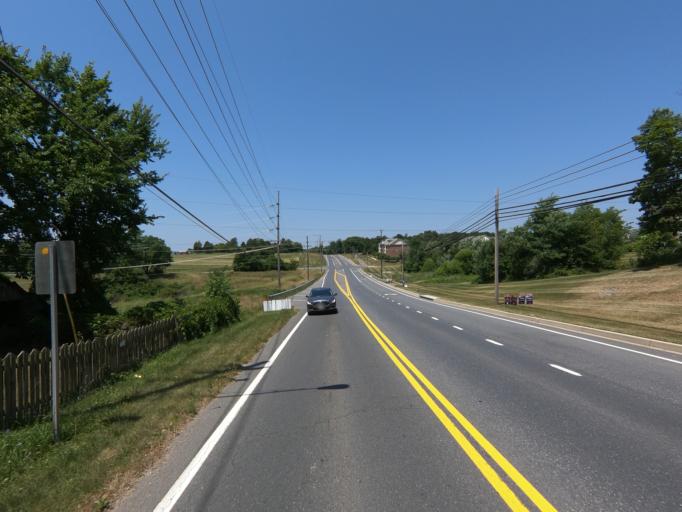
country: US
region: Maryland
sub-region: Montgomery County
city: Clarksburg
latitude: 39.2433
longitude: -77.2859
